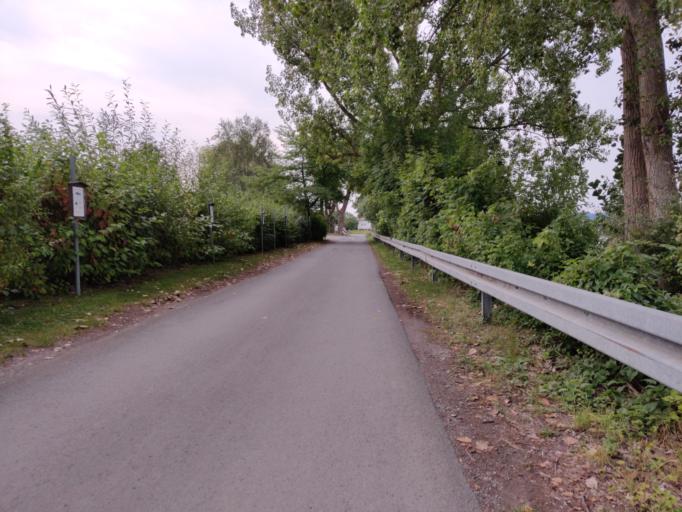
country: DE
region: Lower Saxony
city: Hameln
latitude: 52.0848
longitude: 9.3686
